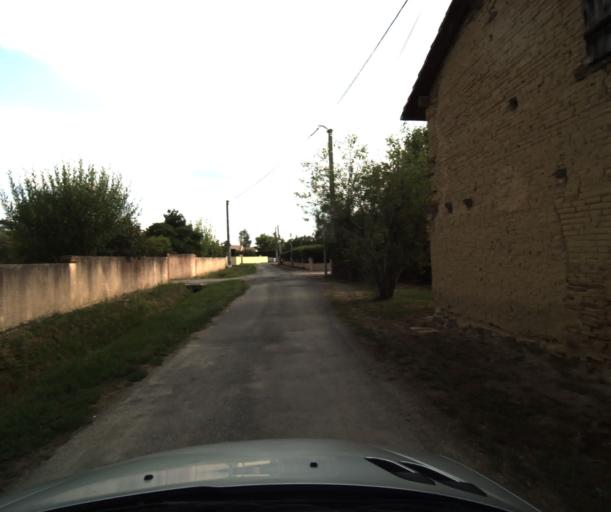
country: FR
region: Midi-Pyrenees
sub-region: Departement de la Haute-Garonne
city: Fonsorbes
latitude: 43.5147
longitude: 1.2131
